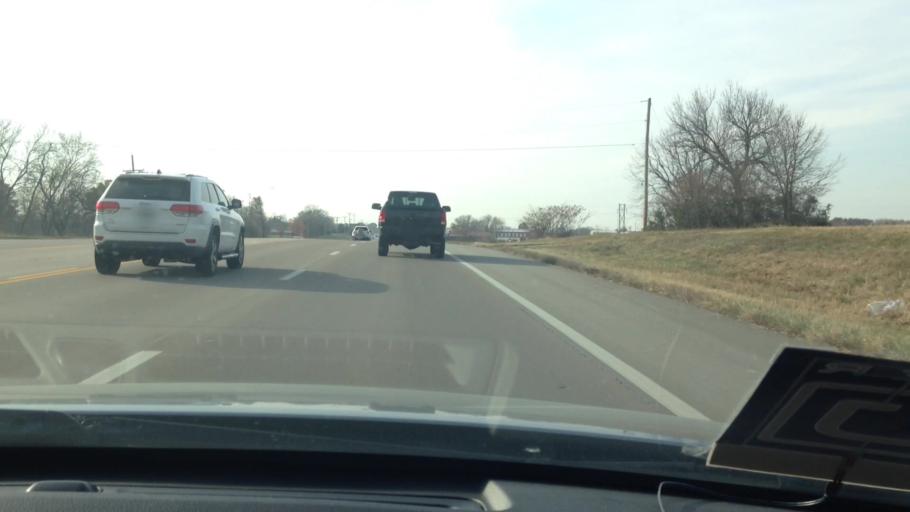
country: US
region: Missouri
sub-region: Henry County
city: Clinton
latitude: 38.3891
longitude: -93.7867
